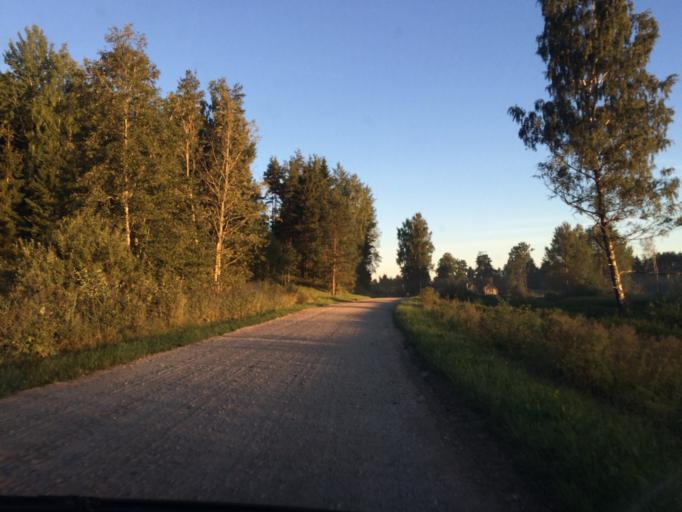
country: LV
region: Preilu Rajons
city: Jaunaglona
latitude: 56.2326
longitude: 27.2177
